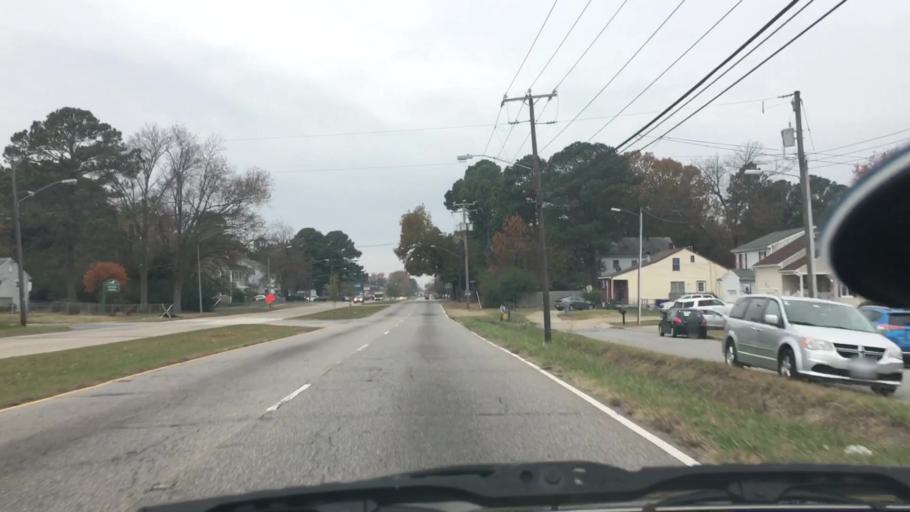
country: US
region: Virginia
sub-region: City of Norfolk
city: Norfolk
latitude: 36.8725
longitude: -76.2211
